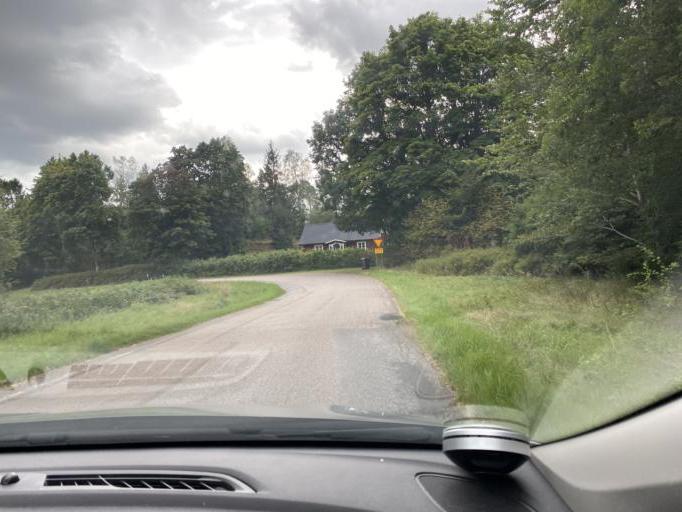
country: SE
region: Kronoberg
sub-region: Markaryds Kommun
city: Markaryd
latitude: 56.4723
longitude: 13.5670
